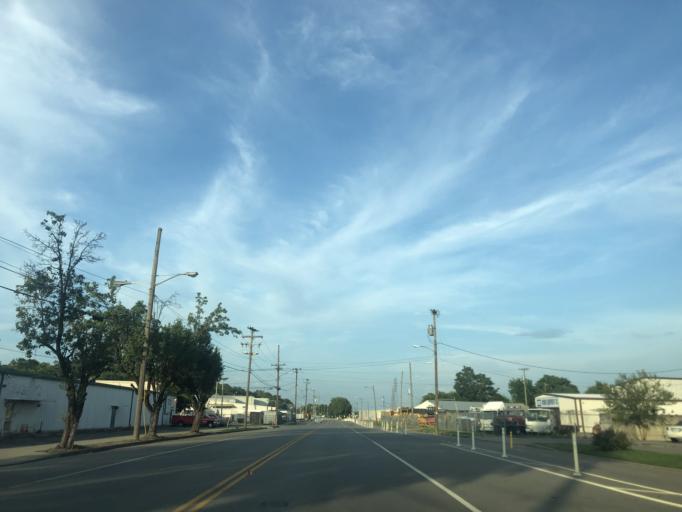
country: US
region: Tennessee
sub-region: Davidson County
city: Nashville
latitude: 36.1612
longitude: -86.7575
